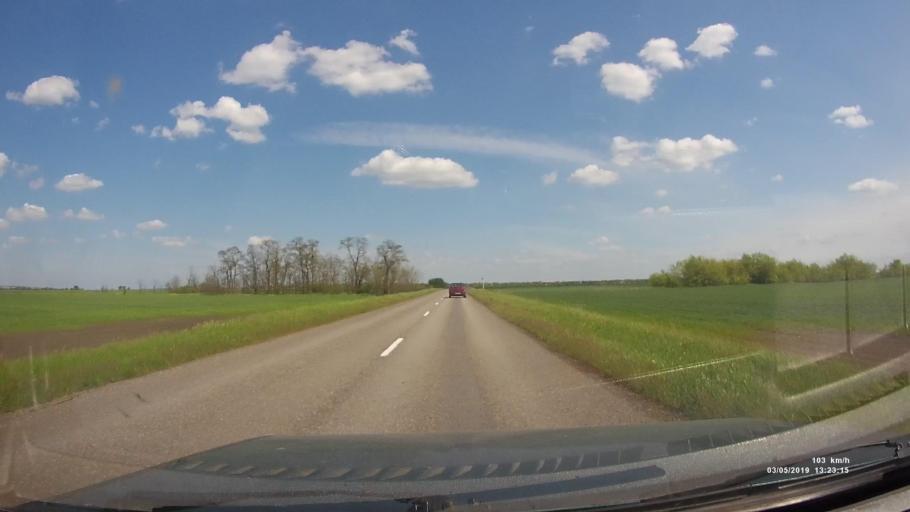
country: RU
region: Rostov
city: Semikarakorsk
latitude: 47.5626
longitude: 40.7777
